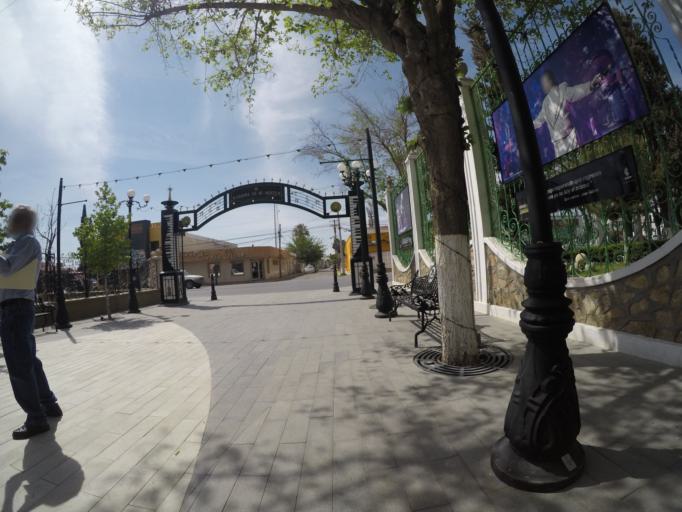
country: MX
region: Chihuahua
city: Ciudad Juarez
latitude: 31.7386
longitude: -106.4693
